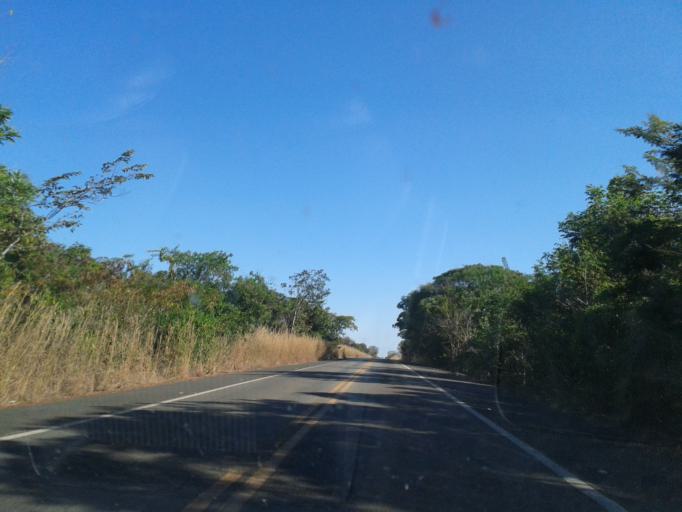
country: BR
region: Goias
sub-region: Mozarlandia
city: Mozarlandia
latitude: -15.0473
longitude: -50.6080
